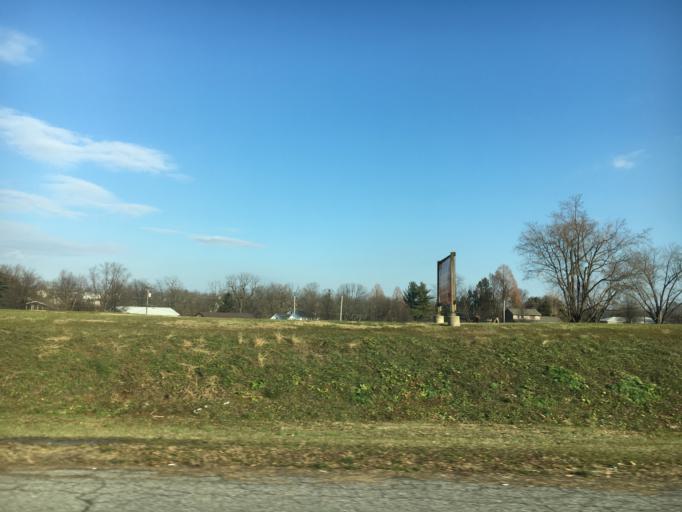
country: US
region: Pennsylvania
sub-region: Lehigh County
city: Stiles
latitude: 40.6588
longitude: -75.5079
